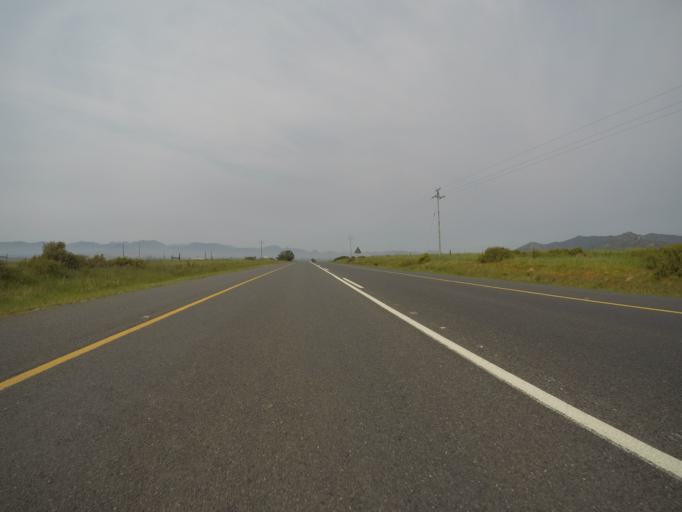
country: ZA
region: Western Cape
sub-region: West Coast District Municipality
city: Malmesbury
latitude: -33.5290
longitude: 18.8494
